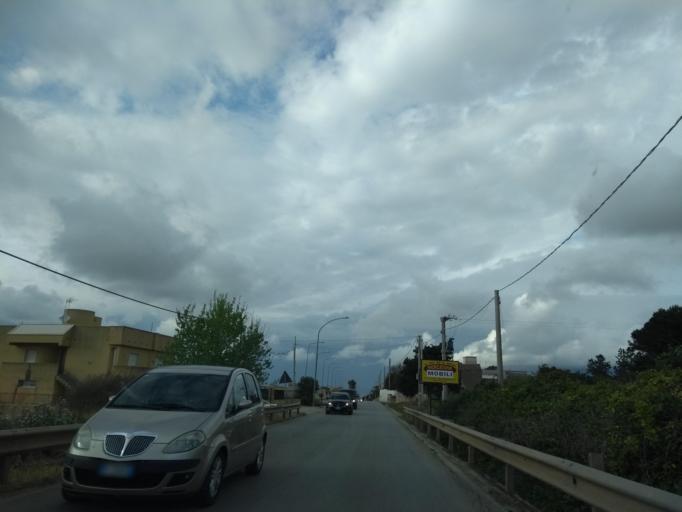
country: IT
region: Sicily
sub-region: Trapani
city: Marausa
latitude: 37.9547
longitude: 12.5161
